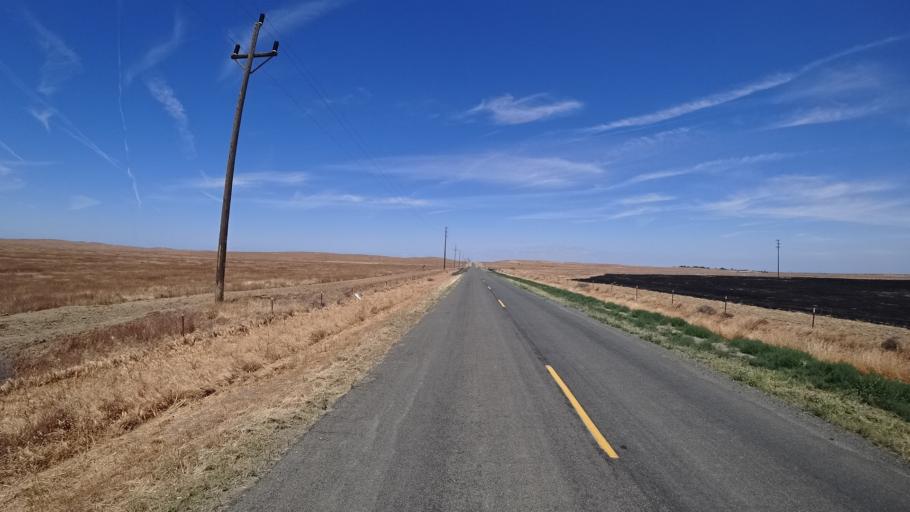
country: US
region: California
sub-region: Kings County
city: Kettleman City
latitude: 35.8416
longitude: -119.9153
